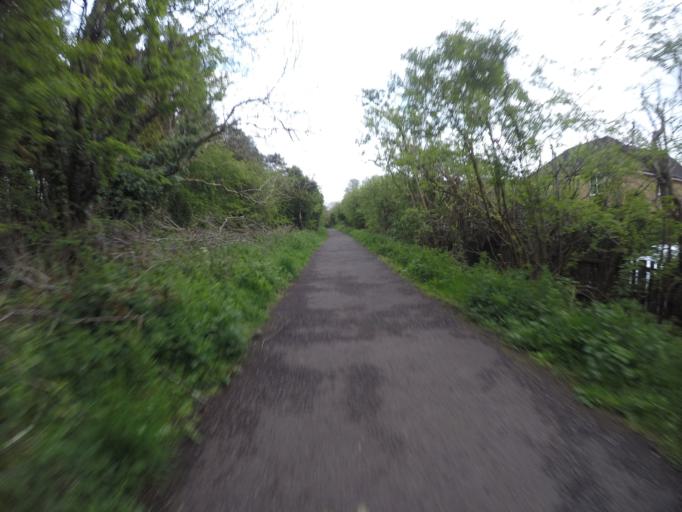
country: GB
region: Scotland
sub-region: North Ayrshire
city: Irvine
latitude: 55.6358
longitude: -4.6343
